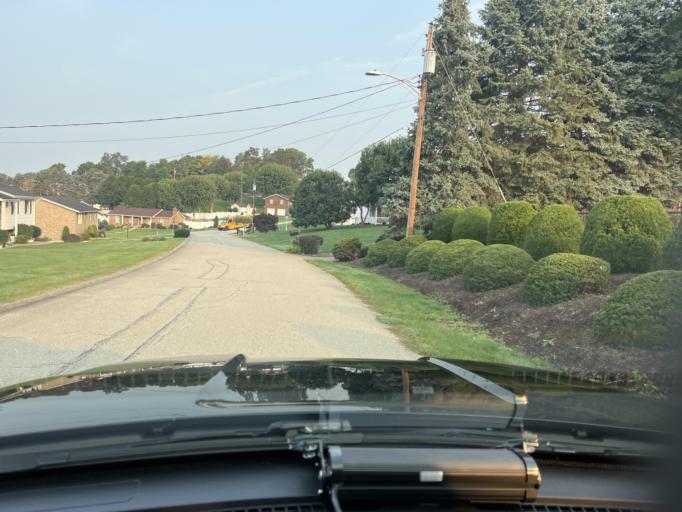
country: US
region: Pennsylvania
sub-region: Fayette County
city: South Uniontown
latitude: 39.8966
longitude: -79.7595
